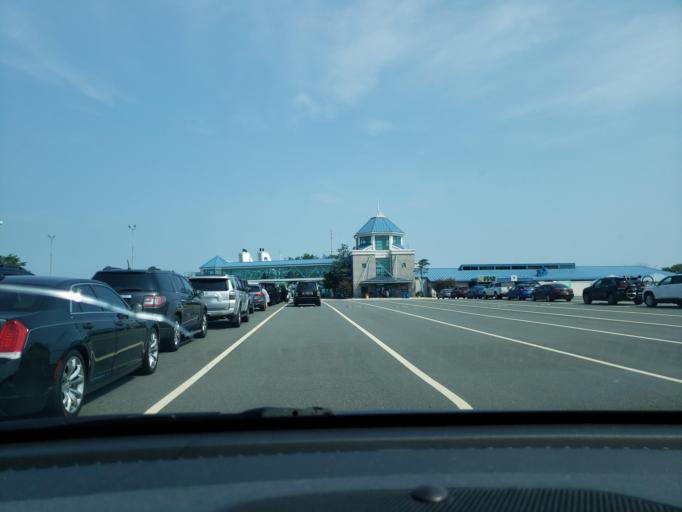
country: US
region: Delaware
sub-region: Sussex County
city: Lewes
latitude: 38.7809
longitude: -75.1192
